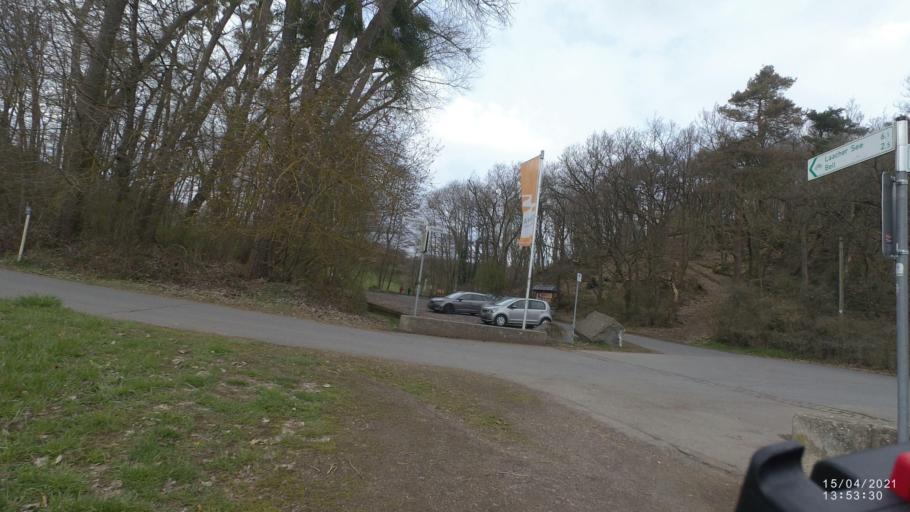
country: DE
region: Rheinland-Pfalz
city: Bell
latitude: 50.3749
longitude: 7.2416
